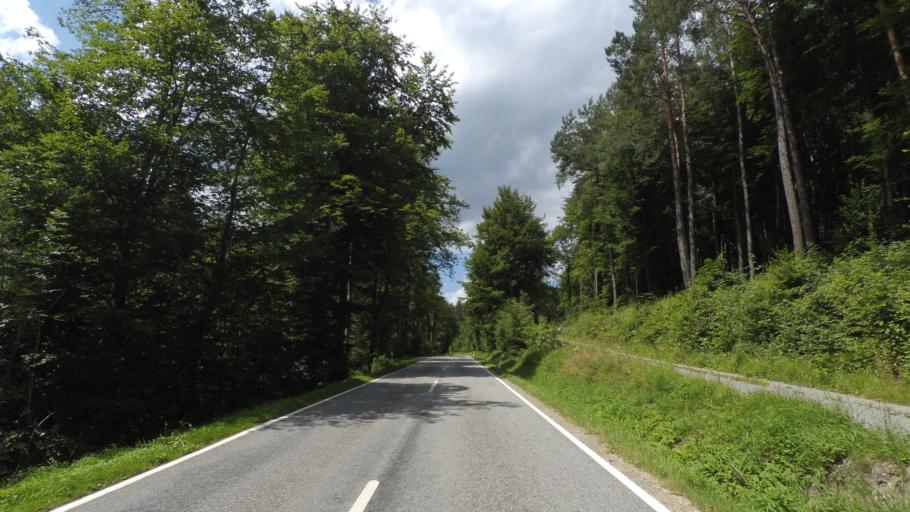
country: DE
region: Baden-Wuerttemberg
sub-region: Regierungsbezirk Stuttgart
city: Lowenstein
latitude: 49.0798
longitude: 9.4157
